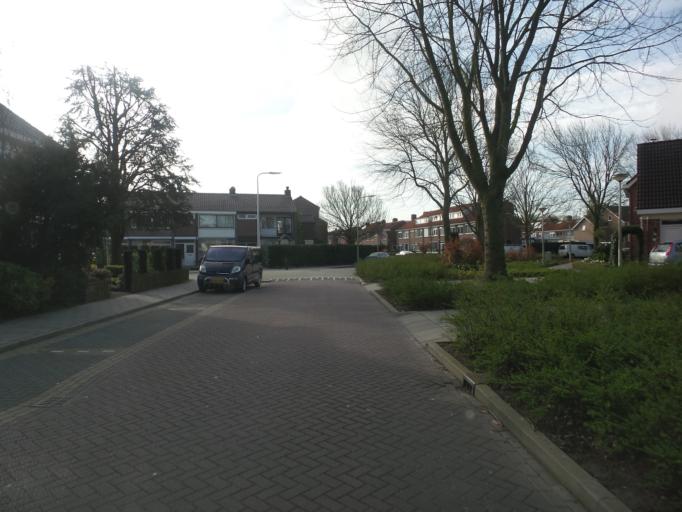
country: NL
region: South Holland
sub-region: Bodegraven-Reeuwijk
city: Bodegraven
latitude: 52.0889
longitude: 4.7441
